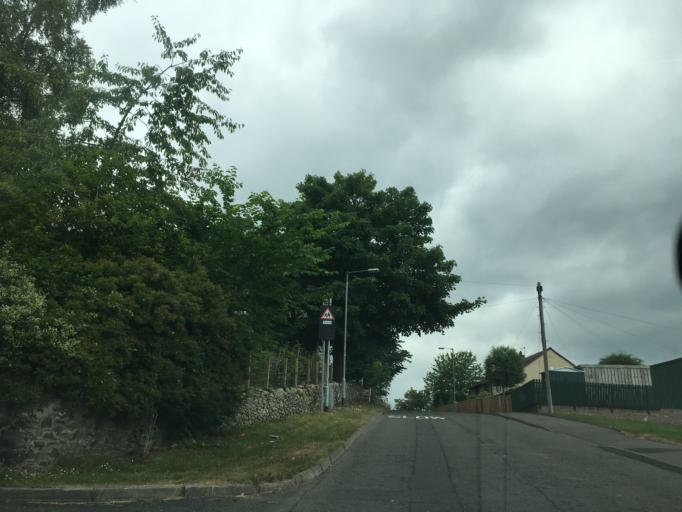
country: GB
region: Scotland
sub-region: The Scottish Borders
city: Peebles
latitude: 55.6437
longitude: -3.1850
